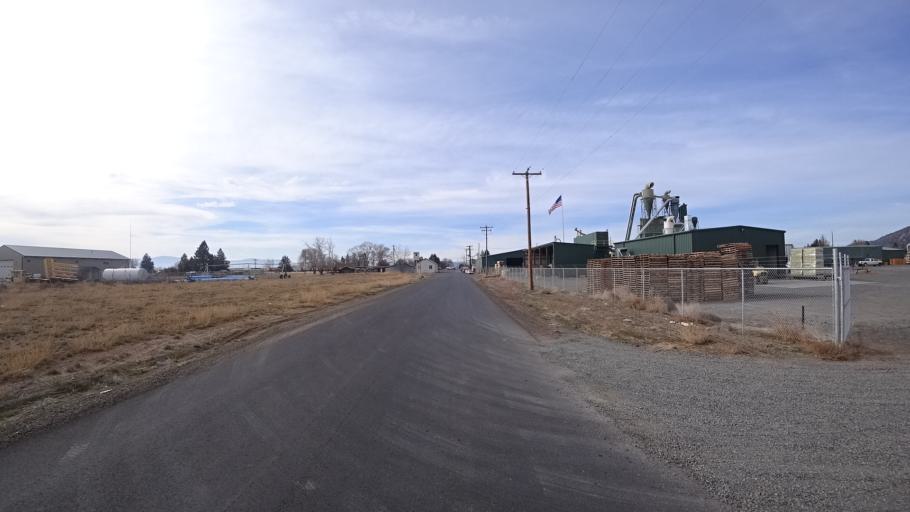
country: US
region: Oregon
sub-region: Klamath County
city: Klamath Falls
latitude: 41.9627
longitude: -121.9145
